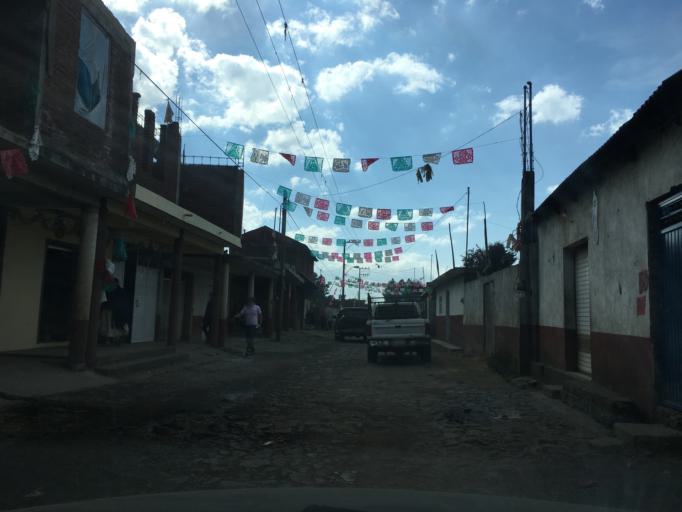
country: MX
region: Michoacan
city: Angahuan
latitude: 19.5472
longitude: -102.2286
